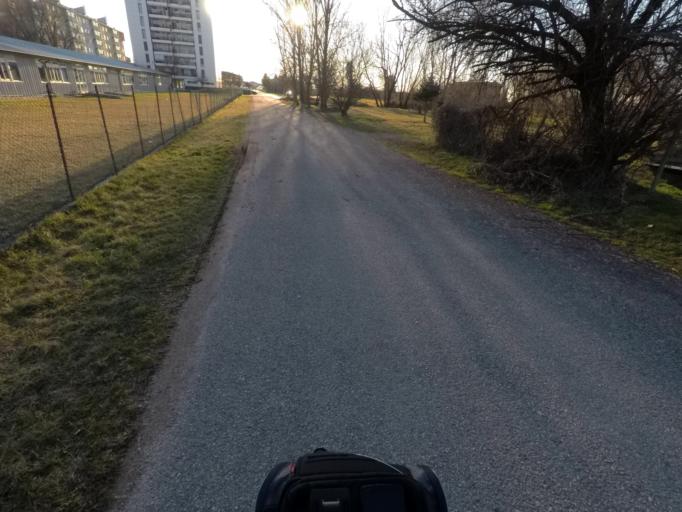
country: IT
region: Friuli Venezia Giulia
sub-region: Provincia di Udine
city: Udine
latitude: 46.0810
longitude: 13.2615
